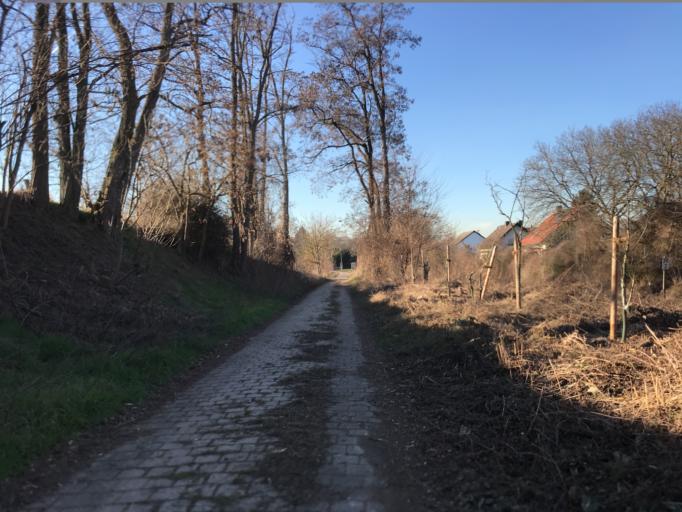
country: DE
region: Rheinland-Pfalz
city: Klein-Winternheim
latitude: 49.9561
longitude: 8.2271
